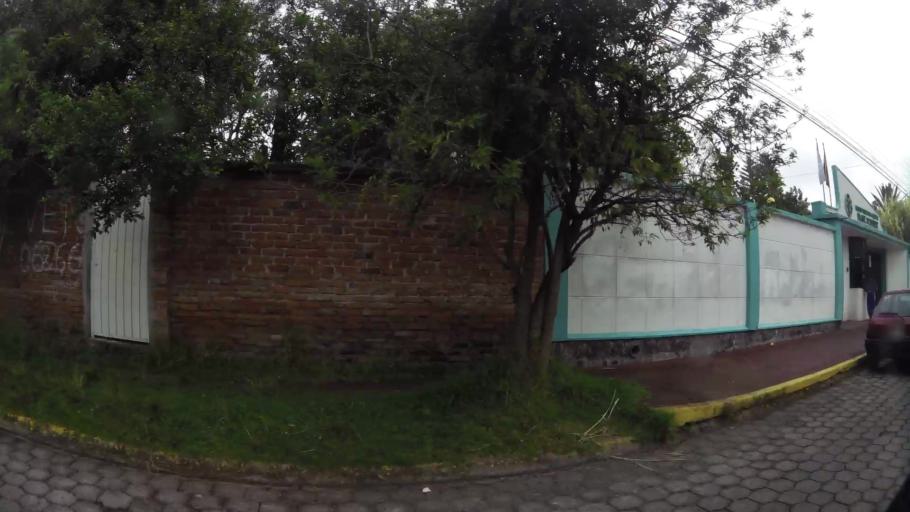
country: EC
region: Pichincha
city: Sangolqui
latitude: -0.2780
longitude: -78.4655
